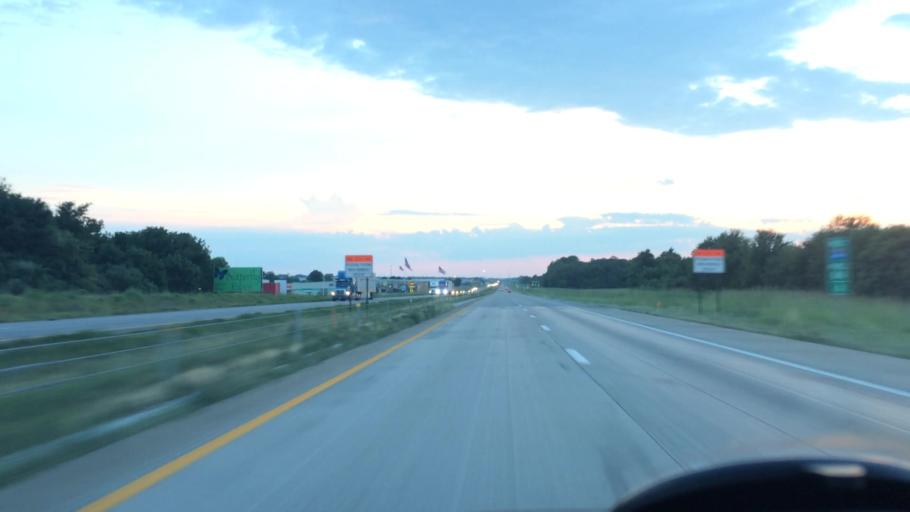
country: US
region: Missouri
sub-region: Greene County
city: Strafford
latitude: 37.2503
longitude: -93.1901
